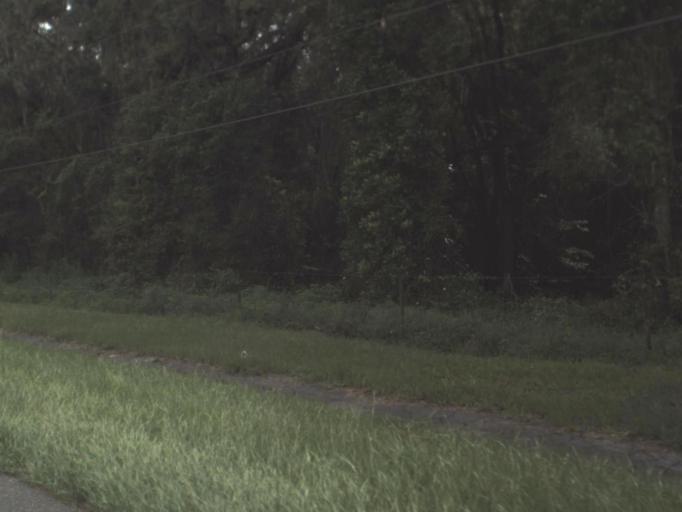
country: US
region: Florida
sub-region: Columbia County
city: Watertown
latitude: 30.0711
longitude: -82.6004
